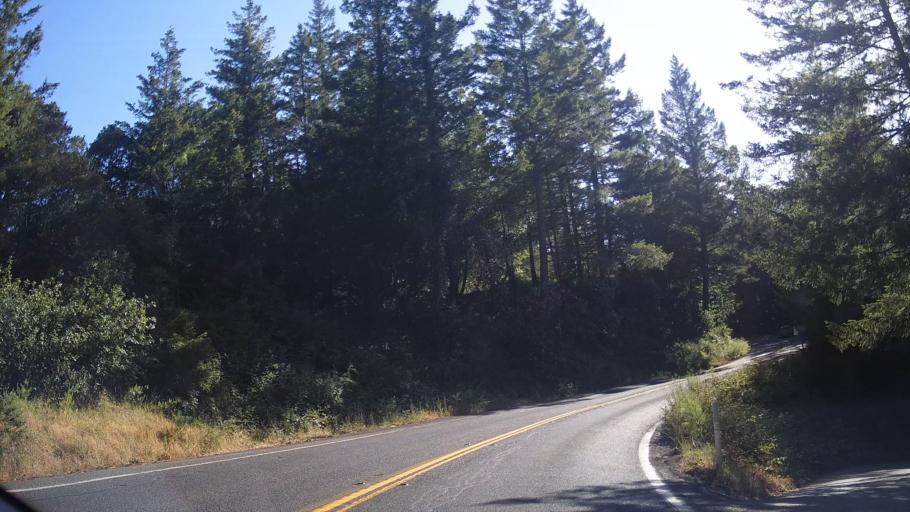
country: US
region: California
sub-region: Mendocino County
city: Brooktrails
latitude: 39.3943
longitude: -123.4556
